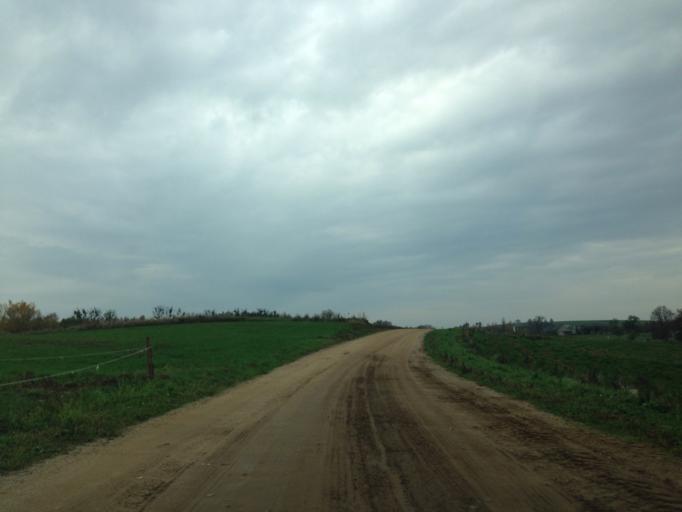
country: PL
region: Kujawsko-Pomorskie
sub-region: Powiat brodnicki
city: Bartniczka
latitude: 53.2836
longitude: 19.6169
